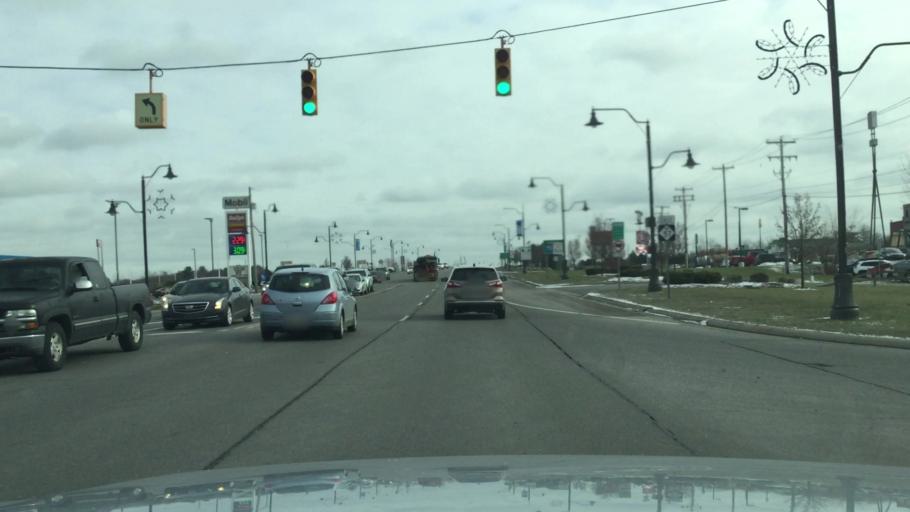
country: US
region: Michigan
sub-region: Genesee County
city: Clio
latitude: 43.1773
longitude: -83.7742
